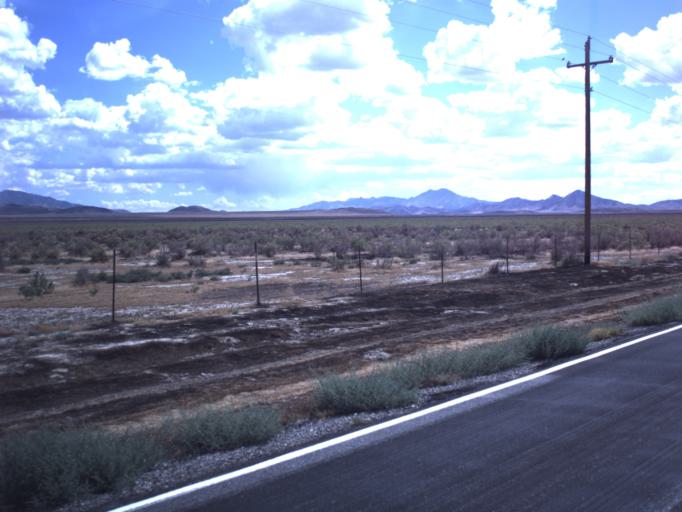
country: US
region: Utah
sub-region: Tooele County
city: Grantsville
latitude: 40.2794
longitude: -112.6718
